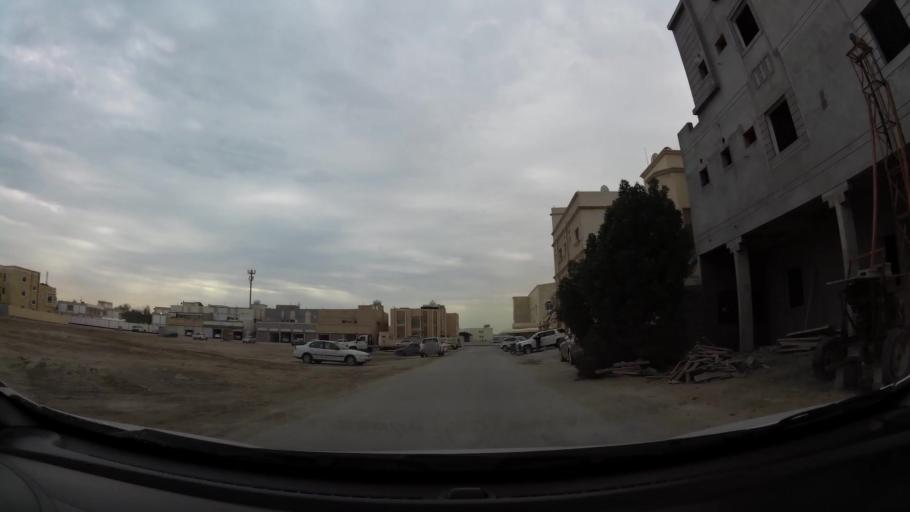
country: BH
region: Northern
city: Sitrah
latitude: 26.1710
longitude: 50.6058
